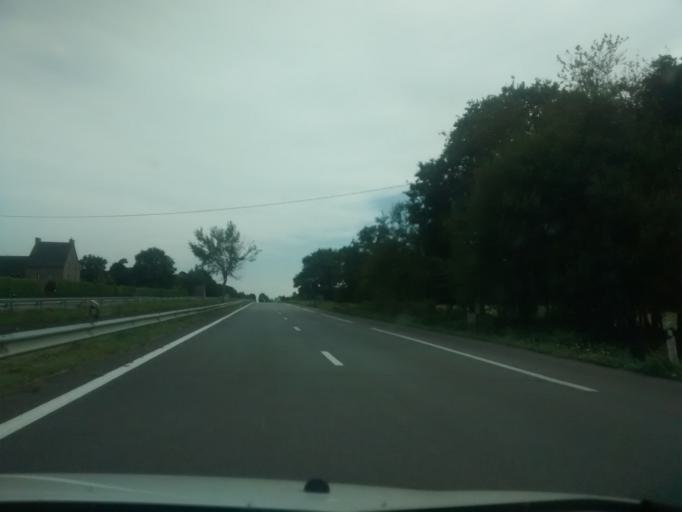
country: FR
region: Brittany
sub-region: Departement d'Ille-et-Vilaine
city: Miniac-Morvan
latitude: 48.4818
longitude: -1.9091
